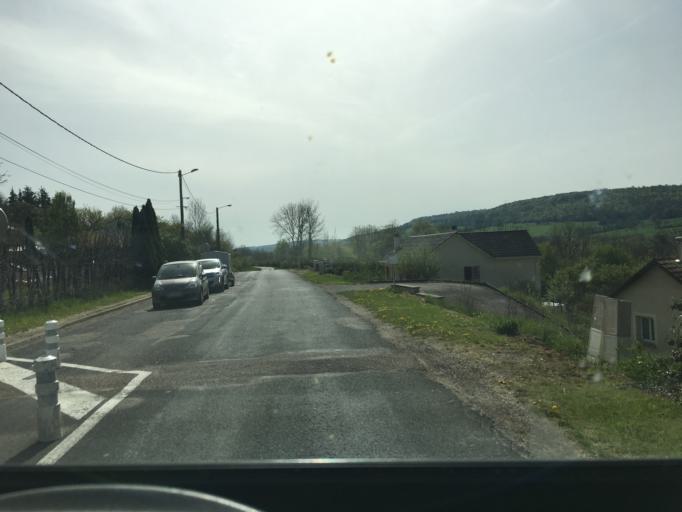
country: FR
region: Lorraine
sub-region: Departement de Meurthe-et-Moselle
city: Chaligny
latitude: 48.6290
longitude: 6.0534
